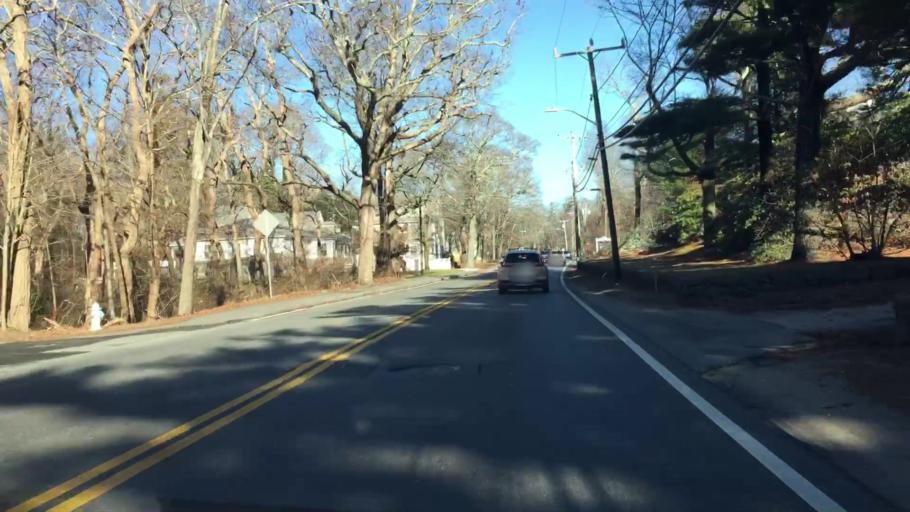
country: US
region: Massachusetts
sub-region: Barnstable County
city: Falmouth
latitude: 41.5653
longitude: -70.6184
